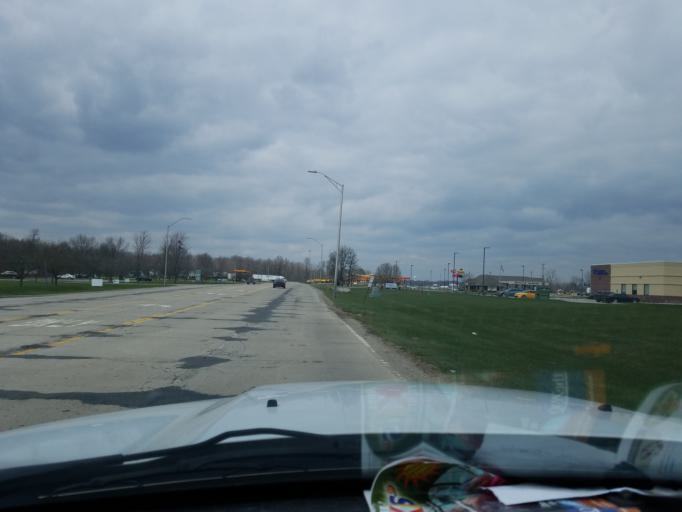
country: US
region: Indiana
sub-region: Sullivan County
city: Farmersburg
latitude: 39.3444
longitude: -87.3904
